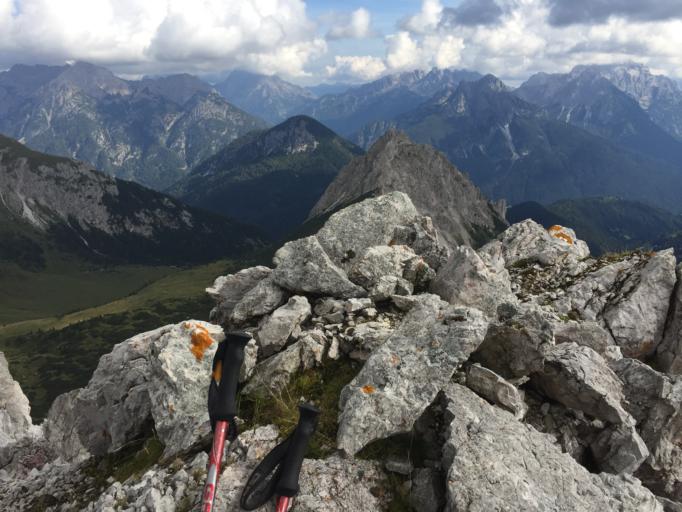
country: IT
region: Veneto
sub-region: Provincia di Belluno
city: San Pietro di Cadore
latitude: 46.6235
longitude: 12.5657
